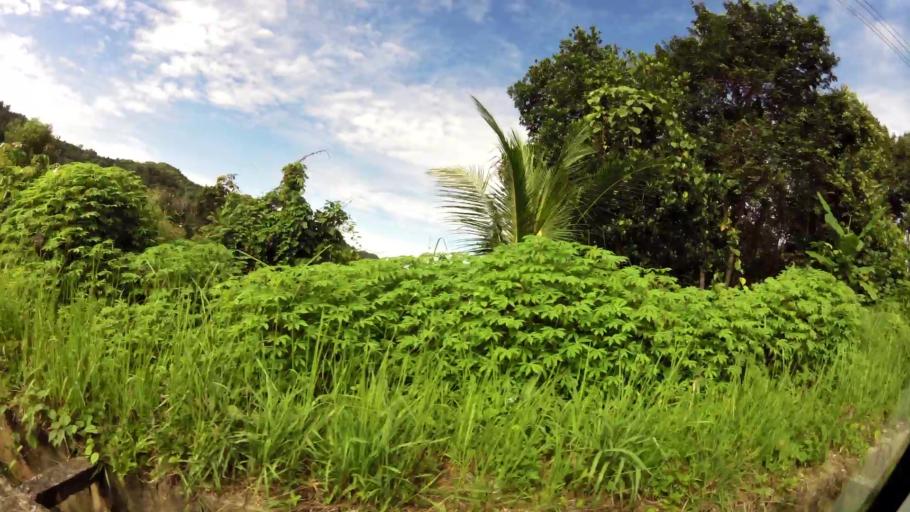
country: BN
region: Brunei and Muara
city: Bandar Seri Begawan
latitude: 4.8963
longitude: 114.9671
